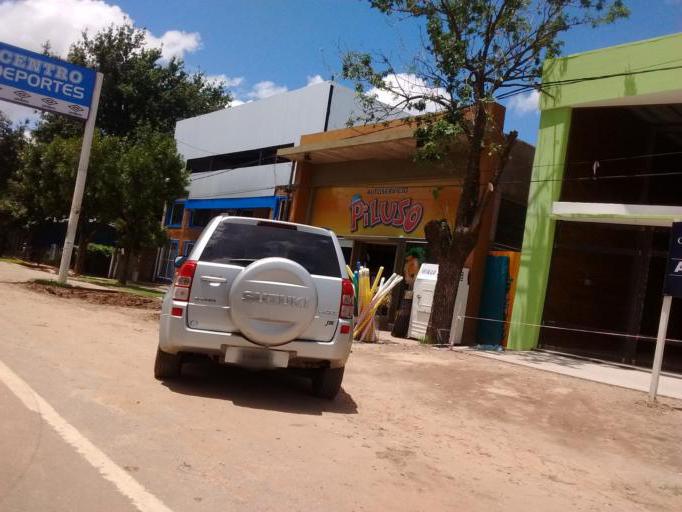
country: AR
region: Santa Fe
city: Funes
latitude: -32.9223
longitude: -60.8071
